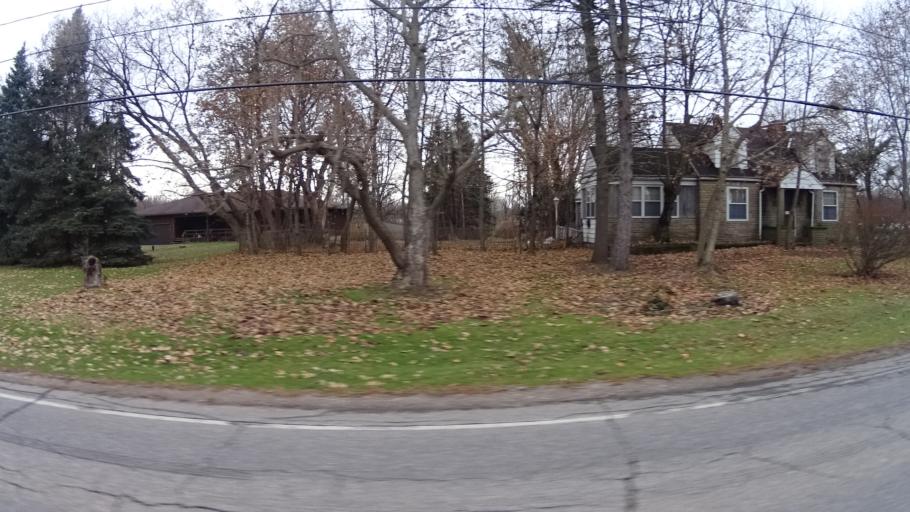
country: US
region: Ohio
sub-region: Lorain County
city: North Ridgeville
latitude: 41.3487
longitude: -82.0287
